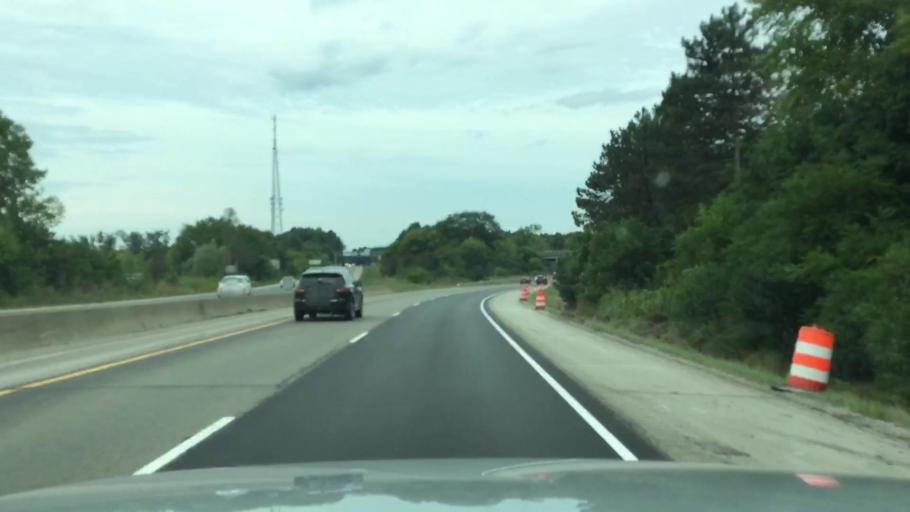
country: US
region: Michigan
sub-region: Washtenaw County
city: Ann Arbor
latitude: 42.2874
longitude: -83.8001
